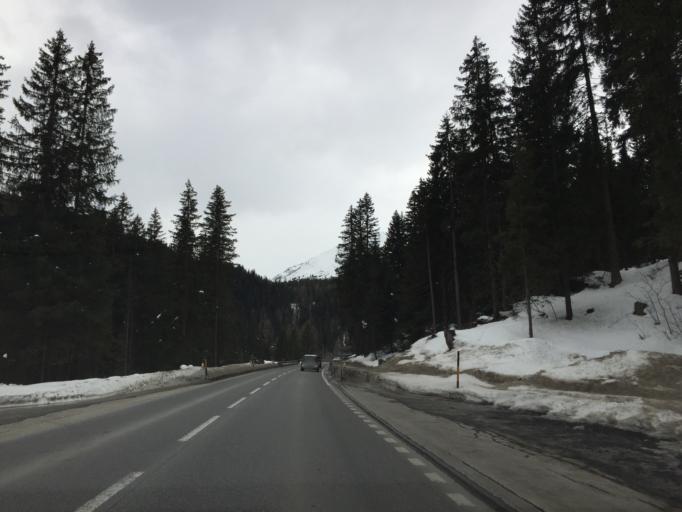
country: CH
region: Grisons
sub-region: Praettigau/Davos District
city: Davos
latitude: 46.8400
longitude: 9.8752
